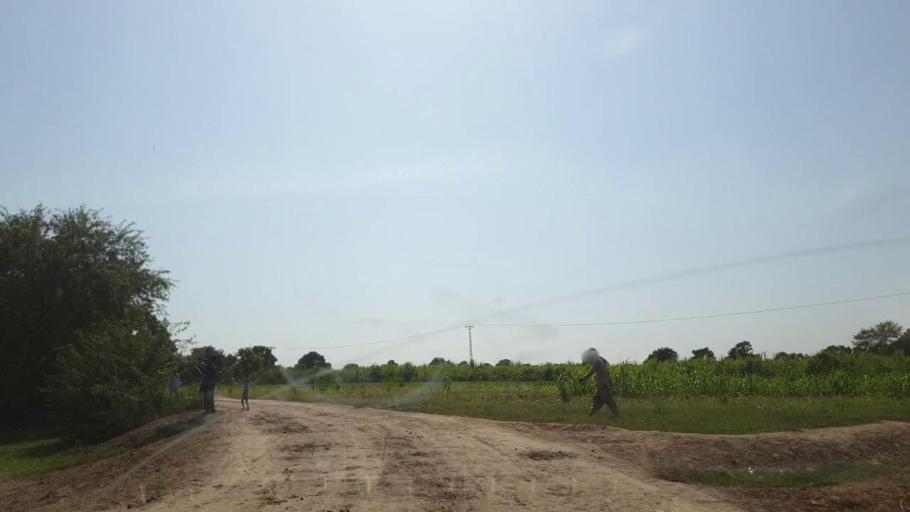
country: PK
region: Sindh
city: Tando Jam
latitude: 25.3788
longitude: 68.5798
